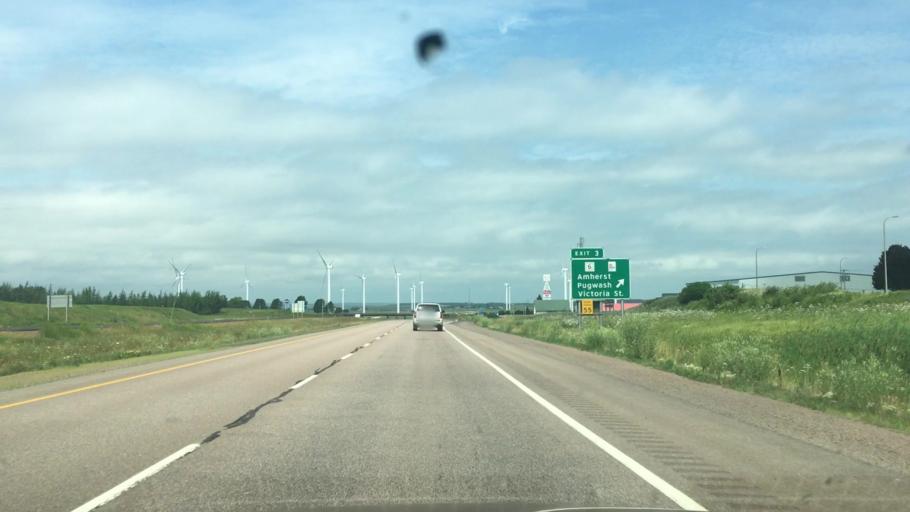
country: CA
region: Nova Scotia
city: Amherst
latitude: 45.8144
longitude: -64.2298
